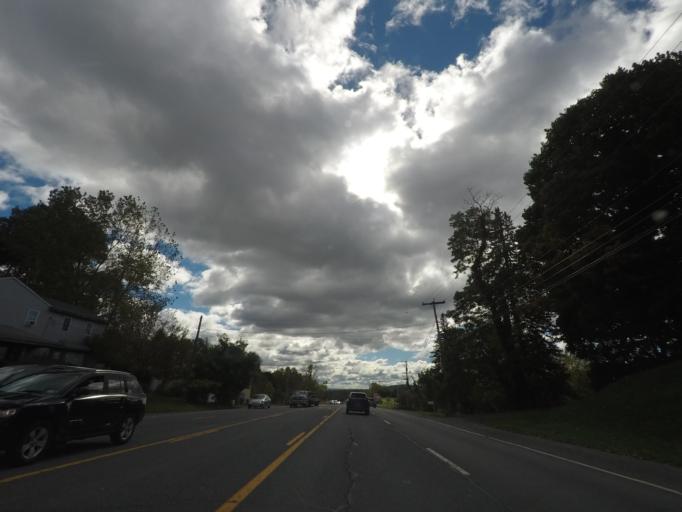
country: US
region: New York
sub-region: Albany County
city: Cohoes
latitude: 42.8279
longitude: -73.7350
